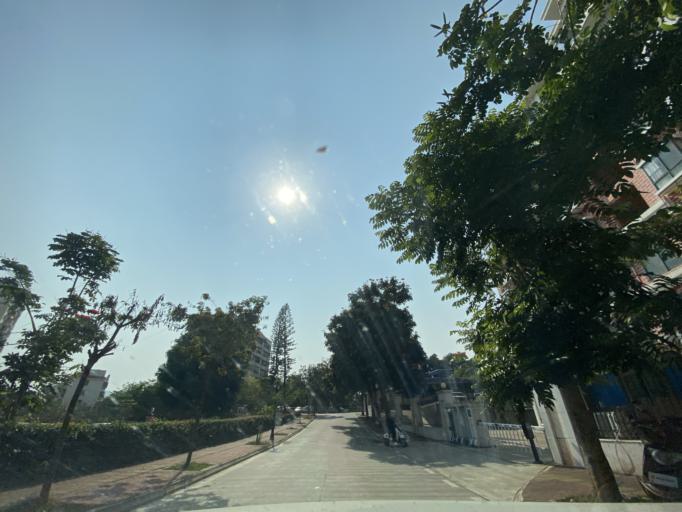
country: CN
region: Hainan
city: Chongshan
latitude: 18.7760
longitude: 109.5137
